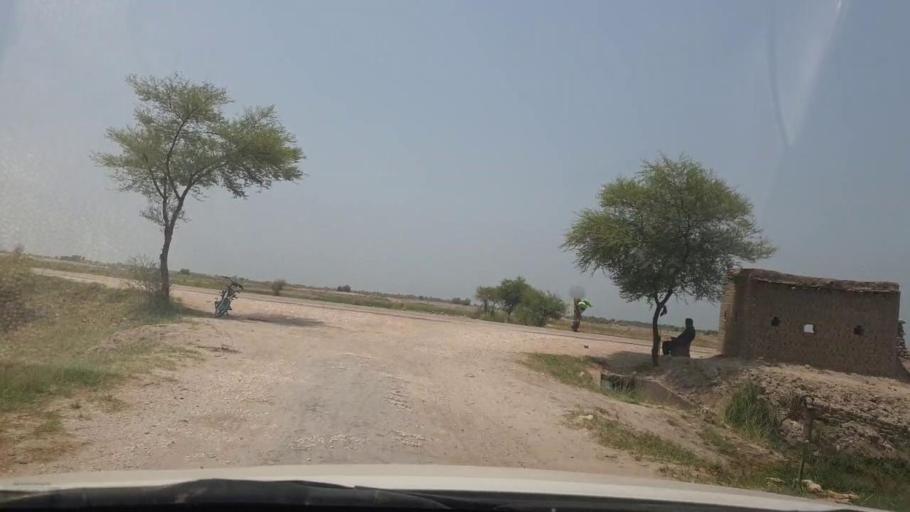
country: PK
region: Sindh
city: Rustam jo Goth
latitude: 28.0533
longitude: 68.7744
